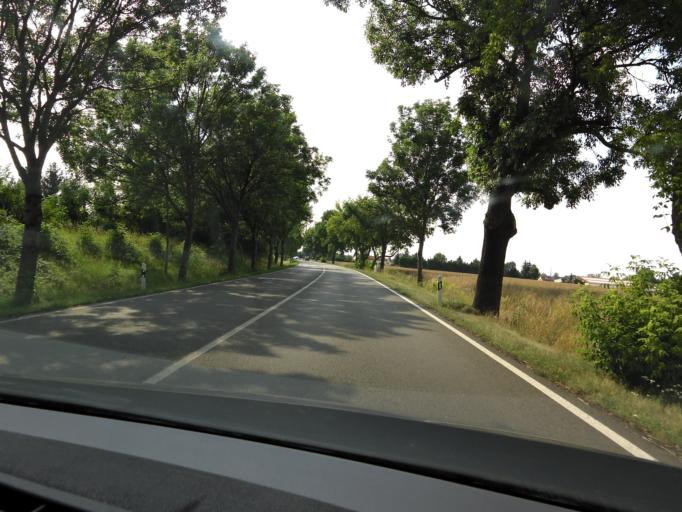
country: DE
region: Saxony
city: Grossposna
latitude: 51.2622
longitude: 12.5108
